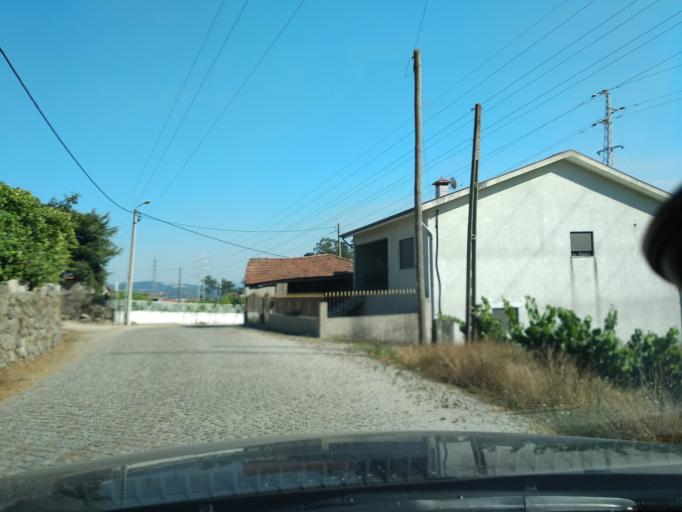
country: PT
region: Porto
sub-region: Paredes
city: Baltar
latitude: 41.2124
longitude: -8.3688
